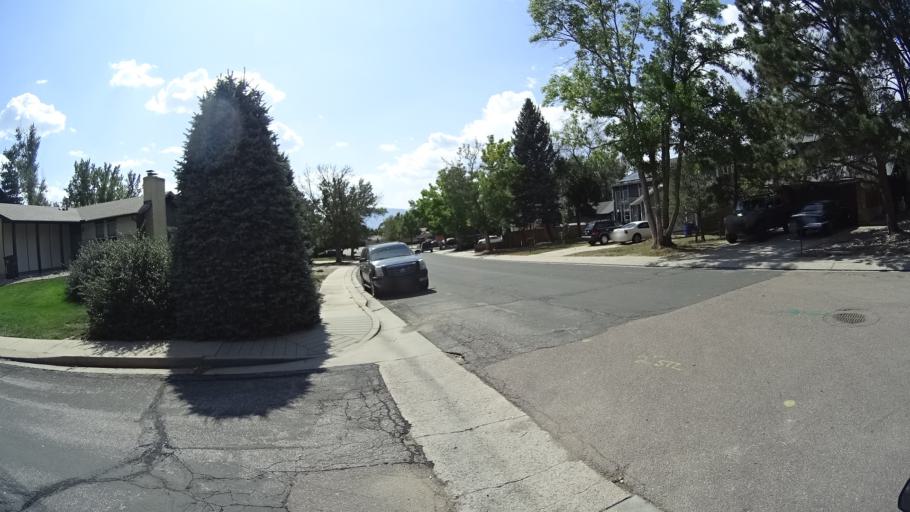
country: US
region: Colorado
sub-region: El Paso County
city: Cimarron Hills
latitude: 38.8751
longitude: -104.7479
